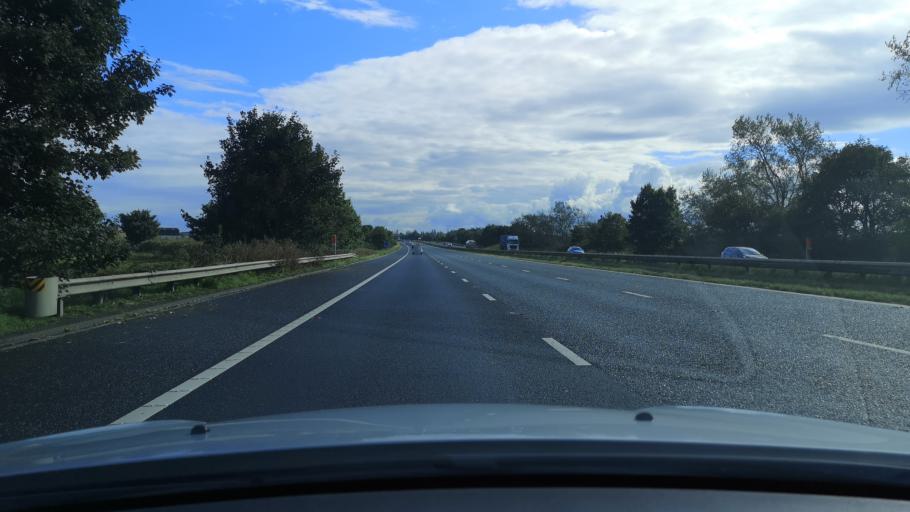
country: GB
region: England
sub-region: East Riding of Yorkshire
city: Pollington
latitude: 53.6870
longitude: -1.0940
